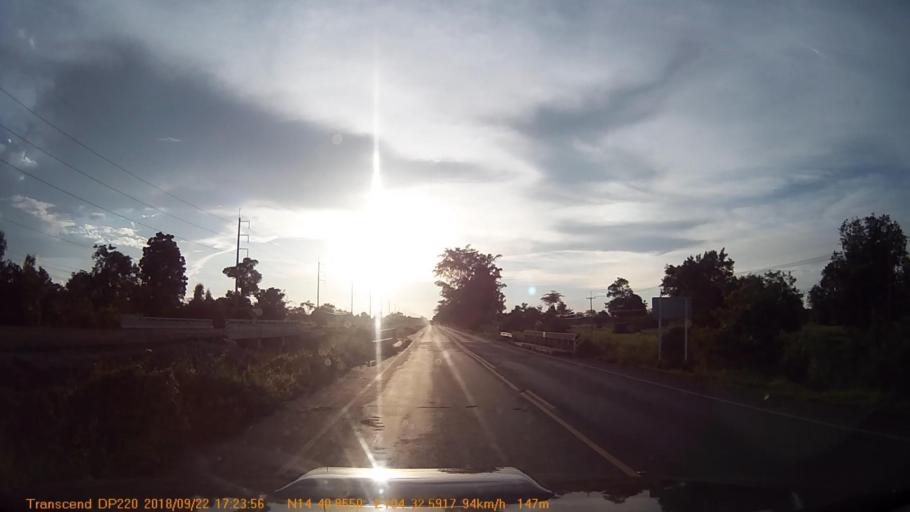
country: TH
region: Sisaket
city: Kantharalak
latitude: 14.6810
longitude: 104.5427
